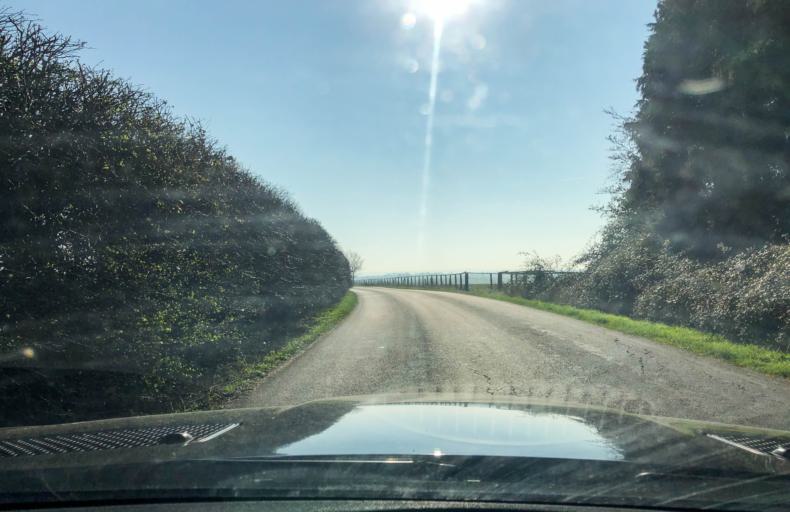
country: GB
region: England
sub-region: Warwickshire
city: Wellesbourne Mountford
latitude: 52.1860
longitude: -1.5392
